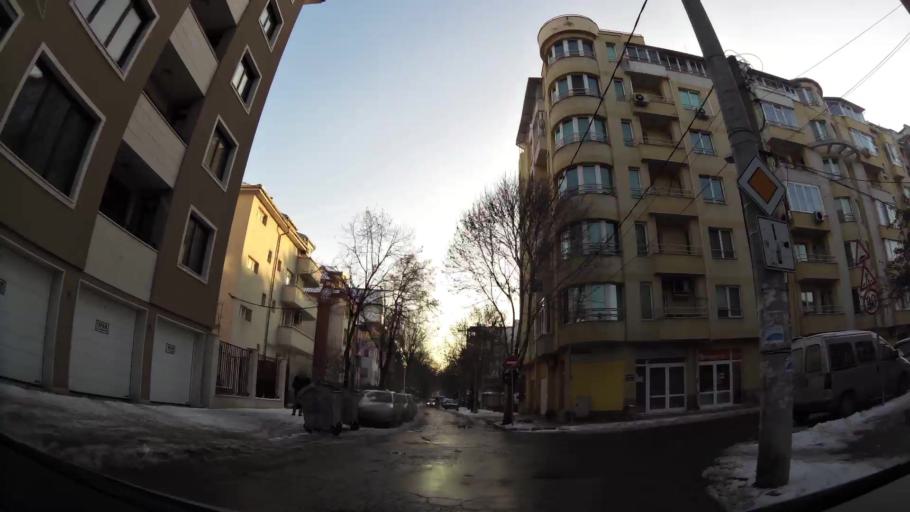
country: BG
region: Sofia-Capital
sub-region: Stolichna Obshtina
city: Sofia
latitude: 42.6890
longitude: 23.3632
